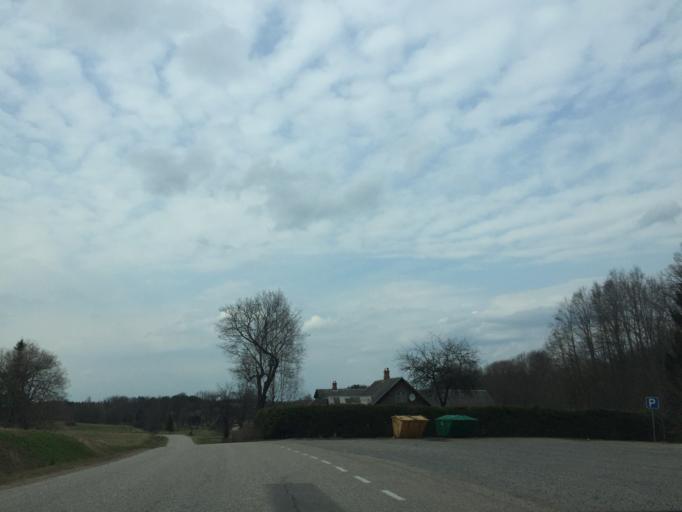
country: EE
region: Vorumaa
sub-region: Voru linn
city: Voru
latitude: 57.7148
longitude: 27.0552
